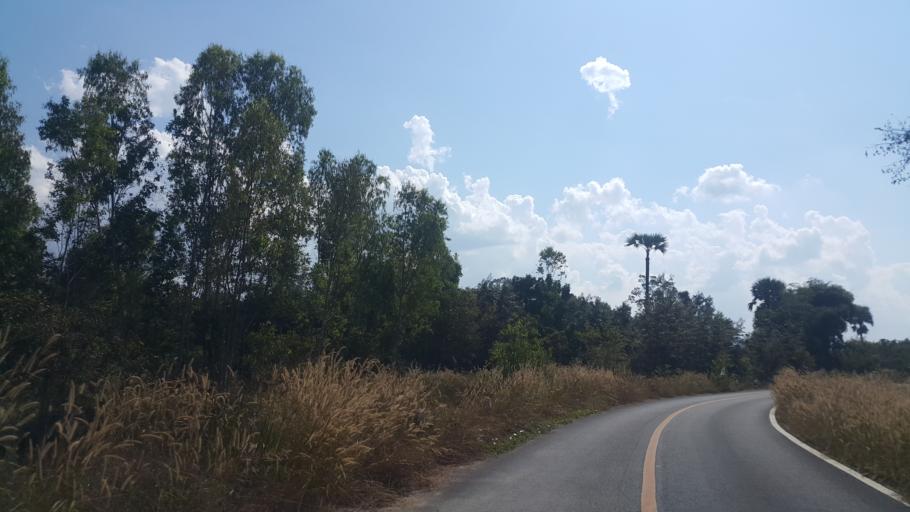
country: TH
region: Lamphun
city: Ban Thi
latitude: 18.6586
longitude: 99.1716
